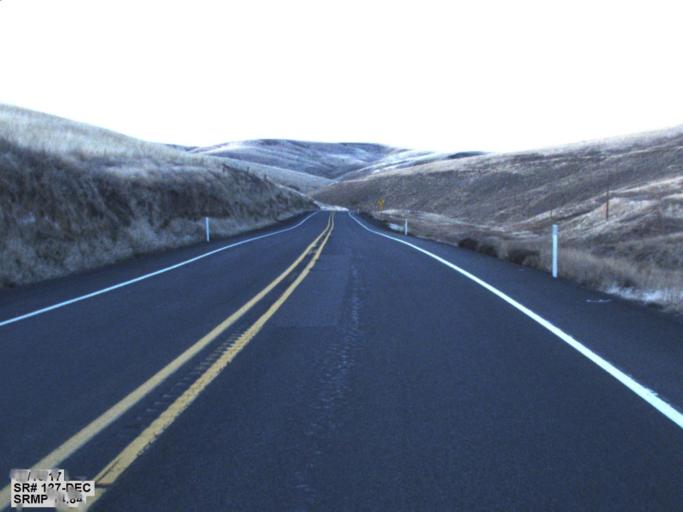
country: US
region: Washington
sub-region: Garfield County
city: Pomeroy
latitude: 46.6833
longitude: -117.8068
